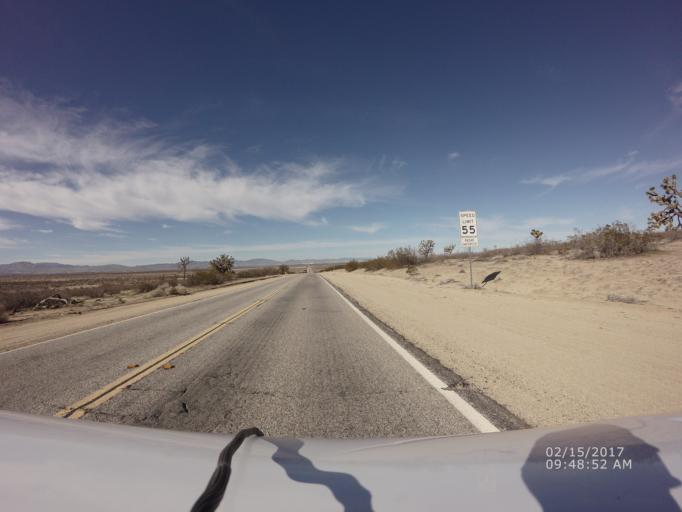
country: US
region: California
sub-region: Los Angeles County
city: Lake Los Angeles
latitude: 34.6167
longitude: -117.9118
